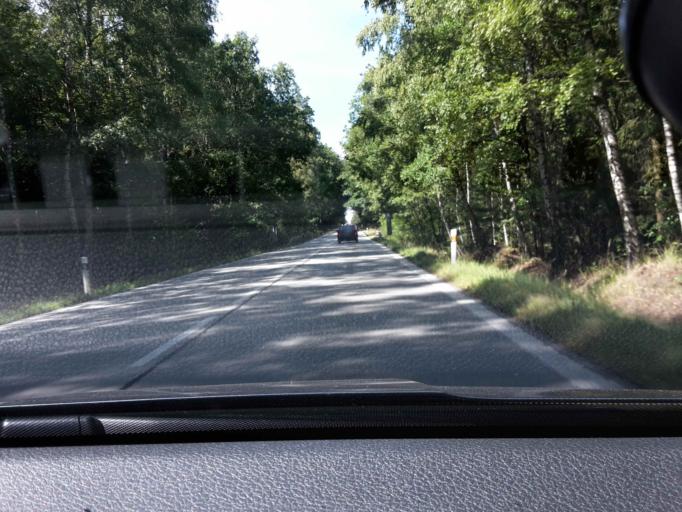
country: CZ
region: Jihocesky
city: Kardasova Recice
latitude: 49.1674
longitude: 14.9181
